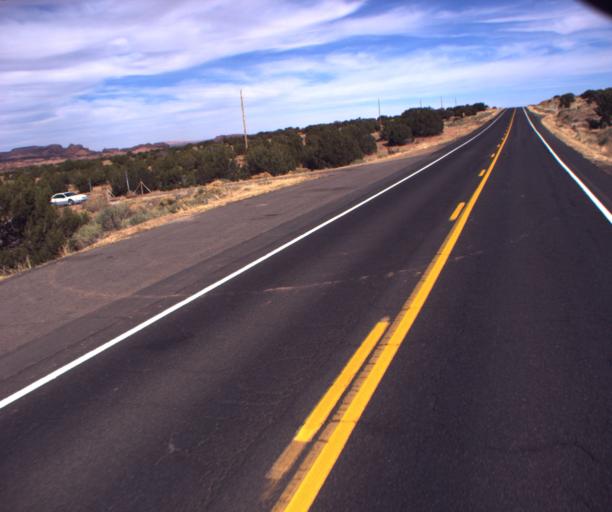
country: US
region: Arizona
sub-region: Navajo County
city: Kayenta
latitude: 36.6964
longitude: -110.3474
